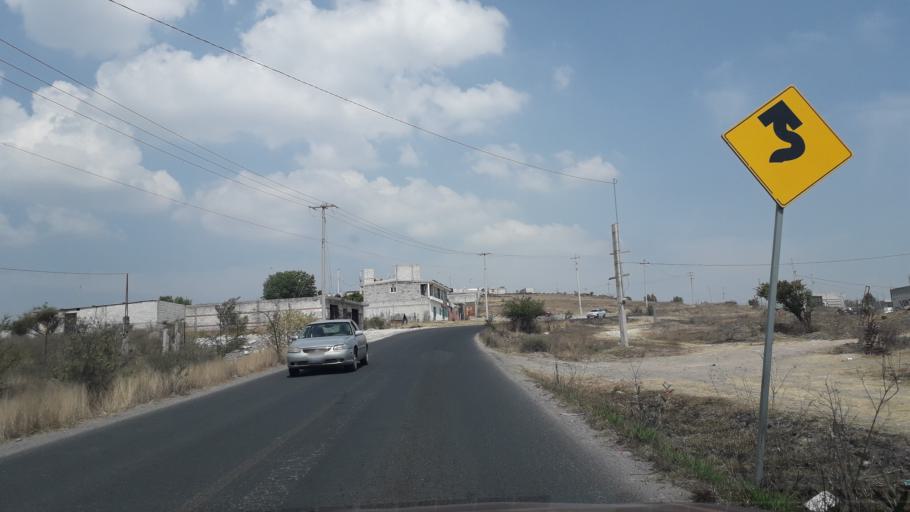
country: MX
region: Puebla
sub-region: Puebla
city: El Capulo (La Quebradora)
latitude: 18.9292
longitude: -98.2580
